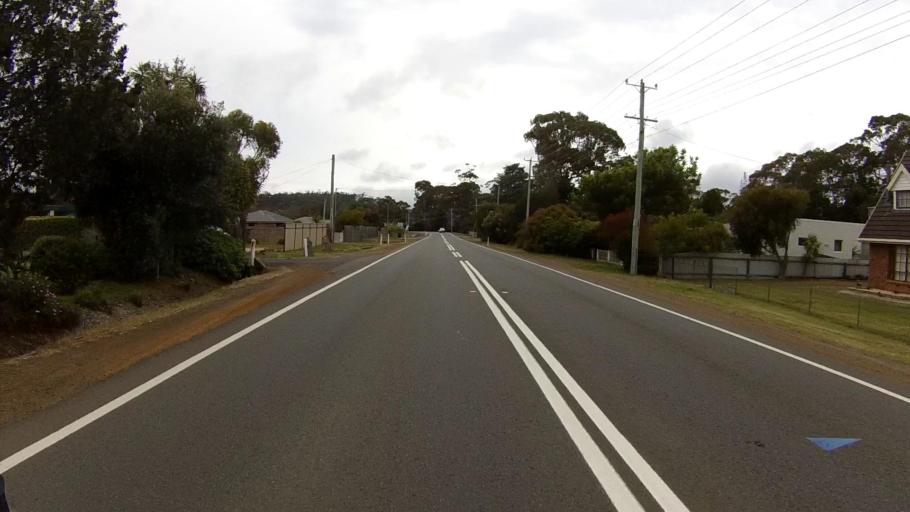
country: AU
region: Tasmania
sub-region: Sorell
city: Sorell
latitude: -42.5506
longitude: 147.8810
